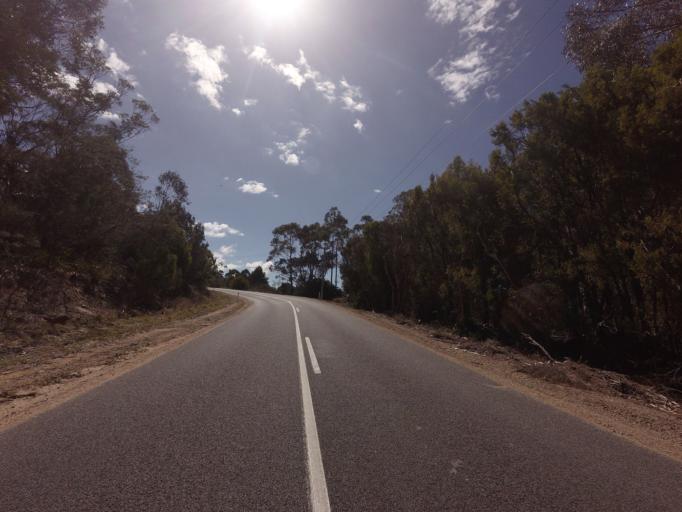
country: AU
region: Tasmania
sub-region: Break O'Day
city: St Helens
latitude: -41.6838
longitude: 148.2819
